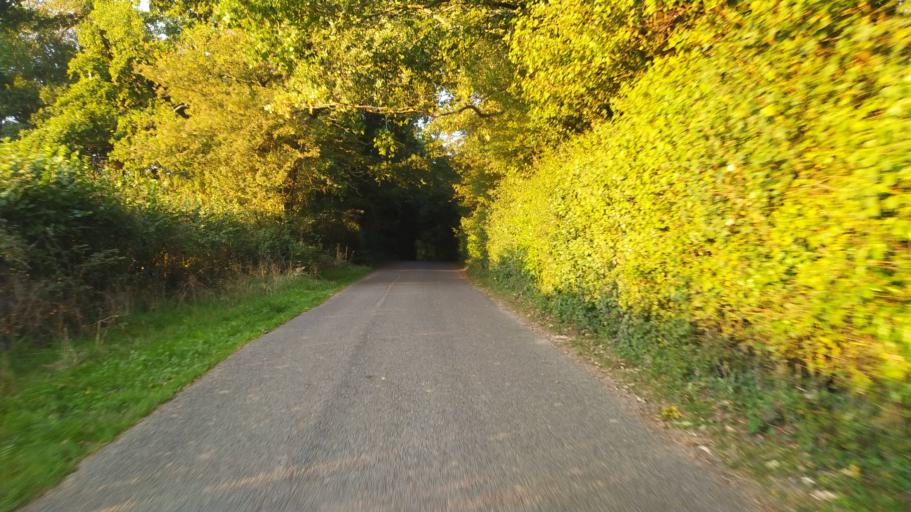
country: GB
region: England
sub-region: Hampshire
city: Lyndhurst
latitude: 50.8621
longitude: -1.5866
